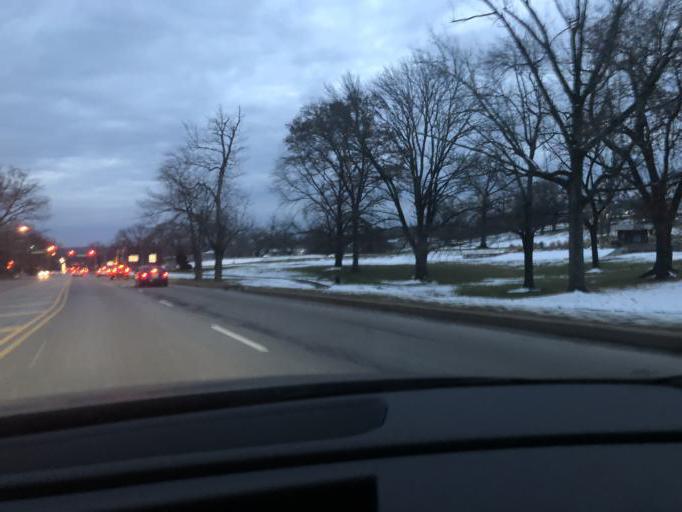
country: US
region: New Jersey
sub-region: Morris County
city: Morristown
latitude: 40.7940
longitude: -74.4424
